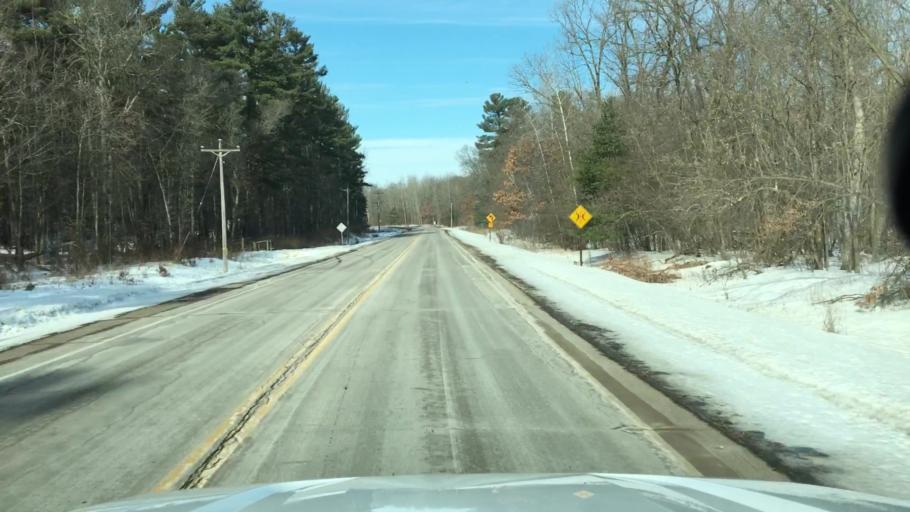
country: US
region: Wisconsin
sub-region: Polk County
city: Saint Croix Falls
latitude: 45.4662
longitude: -92.6867
